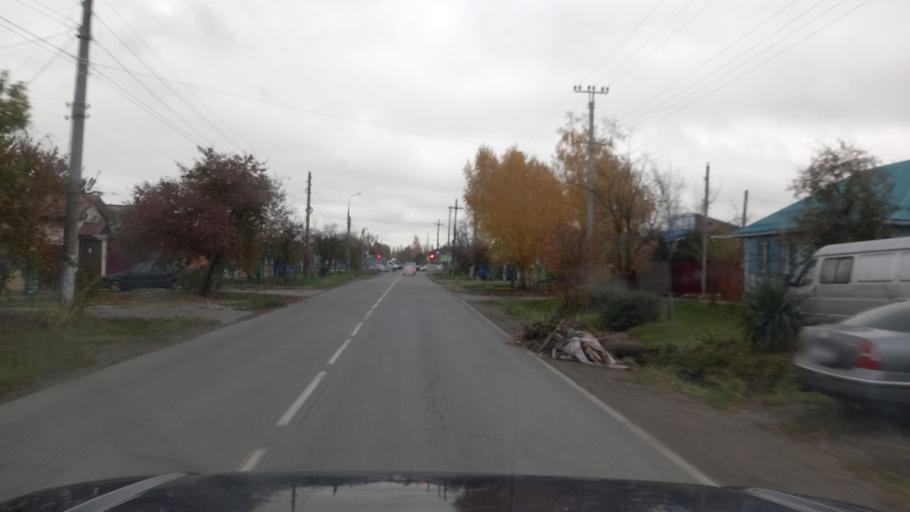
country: RU
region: Adygeya
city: Maykop
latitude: 44.6141
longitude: 40.1277
